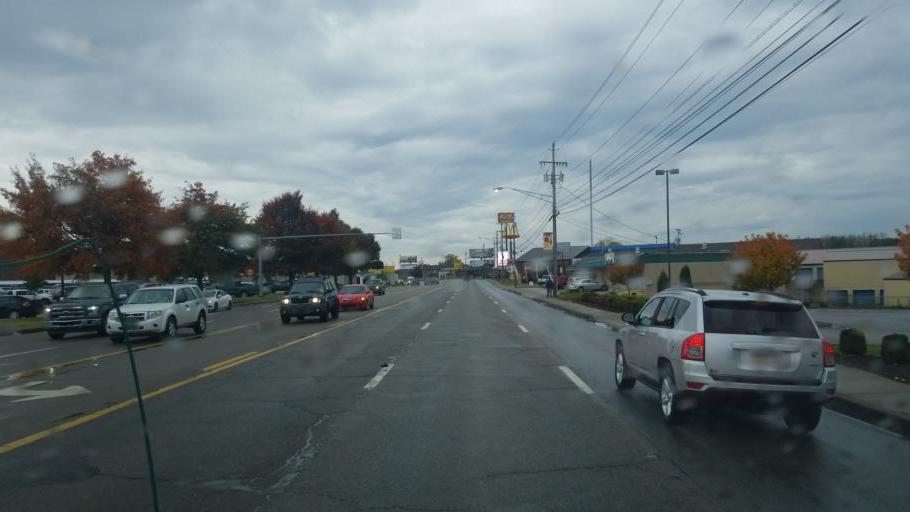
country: US
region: West Virginia
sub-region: Wood County
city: Vienna
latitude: 39.3106
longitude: -81.5530
